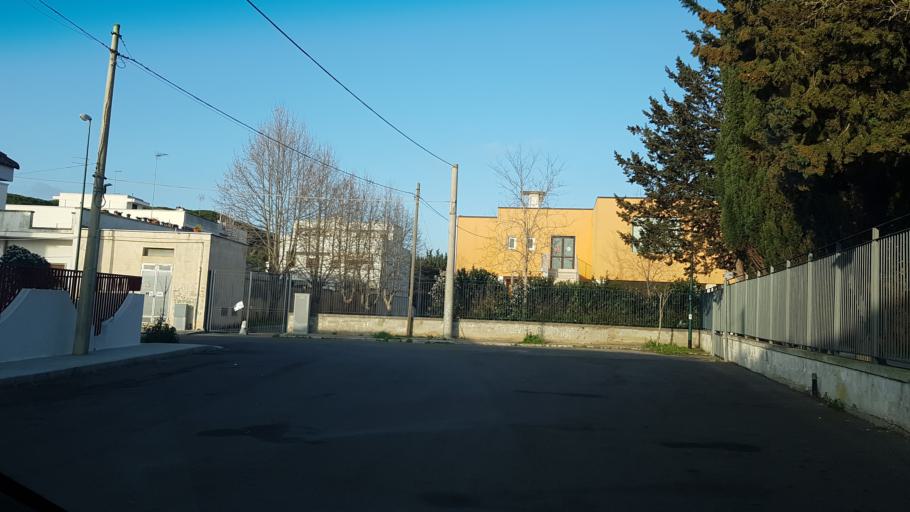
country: IT
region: Apulia
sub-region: Provincia di Lecce
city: Campi Salentina
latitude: 40.3947
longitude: 18.0267
